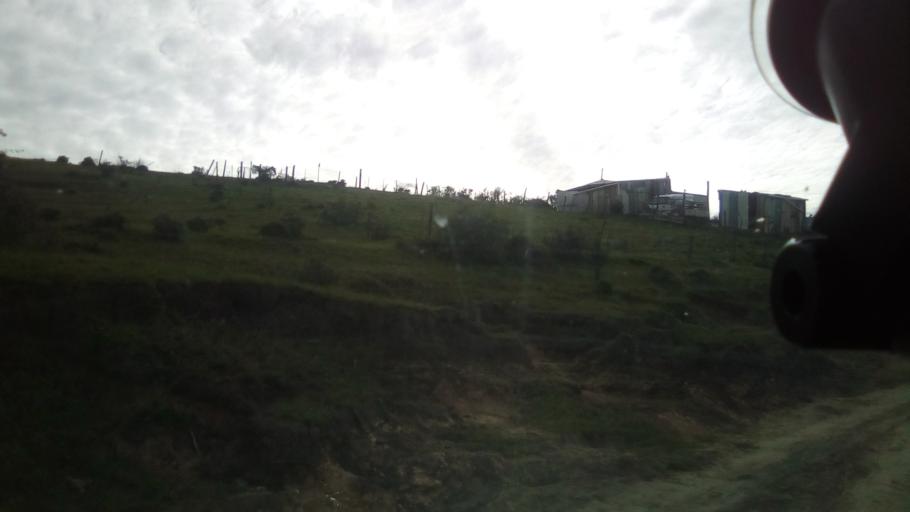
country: ZA
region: Eastern Cape
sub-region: Buffalo City Metropolitan Municipality
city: East London
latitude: -32.7966
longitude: 27.9560
